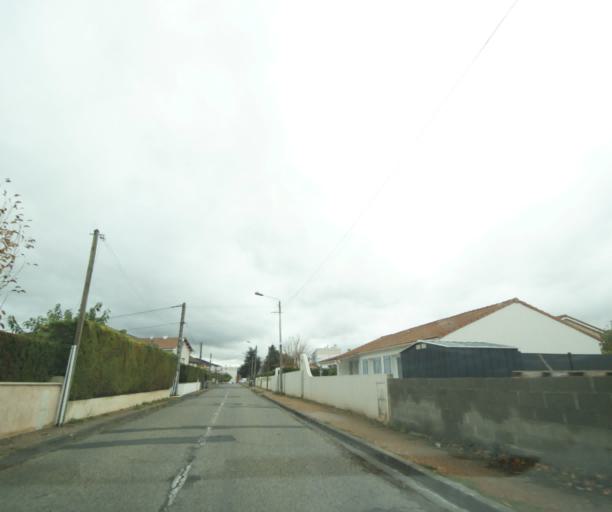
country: FR
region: Auvergne
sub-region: Departement du Puy-de-Dome
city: Pont-du-Chateau
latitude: 45.8054
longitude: 3.2443
